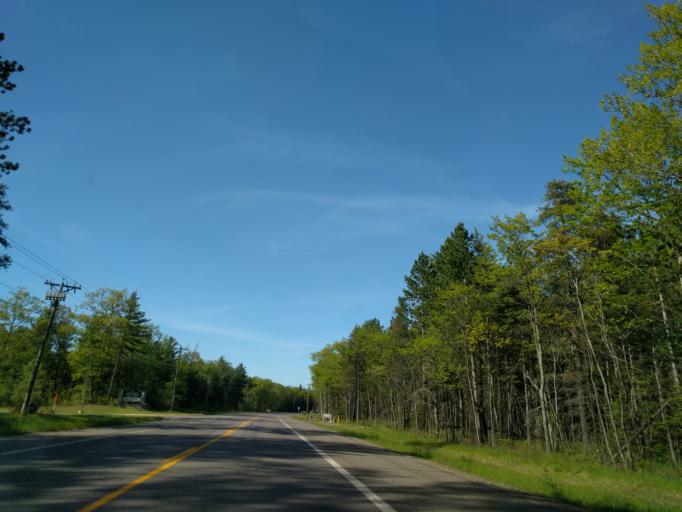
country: US
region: Michigan
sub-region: Marquette County
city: Harvey
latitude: 46.4721
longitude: -87.4235
